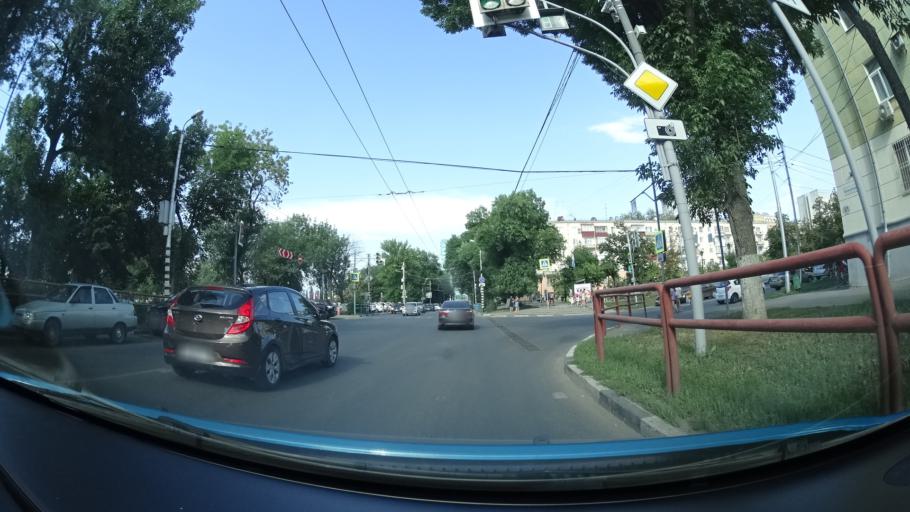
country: RU
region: Samara
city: Samara
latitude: 53.2090
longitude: 50.1179
